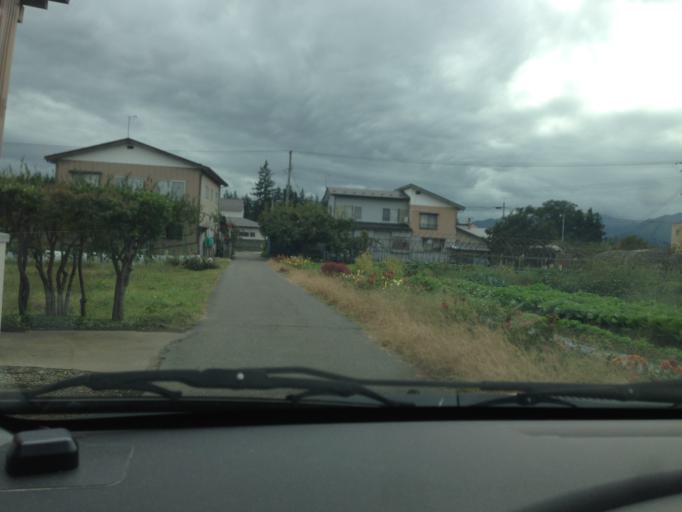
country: JP
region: Fukushima
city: Kitakata
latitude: 37.4655
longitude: 139.8437
